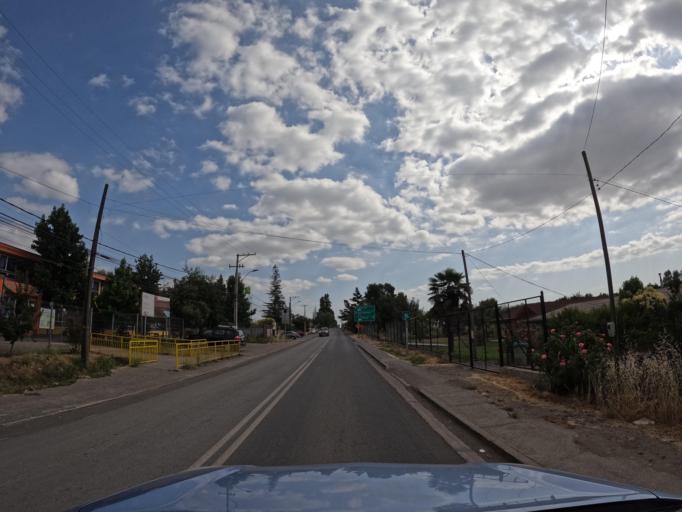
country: CL
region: Maule
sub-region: Provincia de Curico
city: Molina
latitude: -35.1610
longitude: -71.2867
